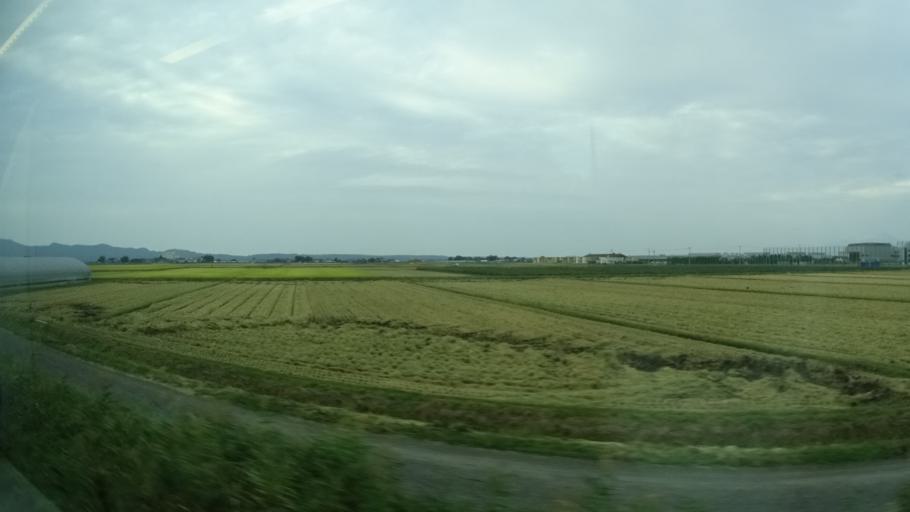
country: JP
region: Yamagata
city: Tsuruoka
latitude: 38.7407
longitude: 139.8233
